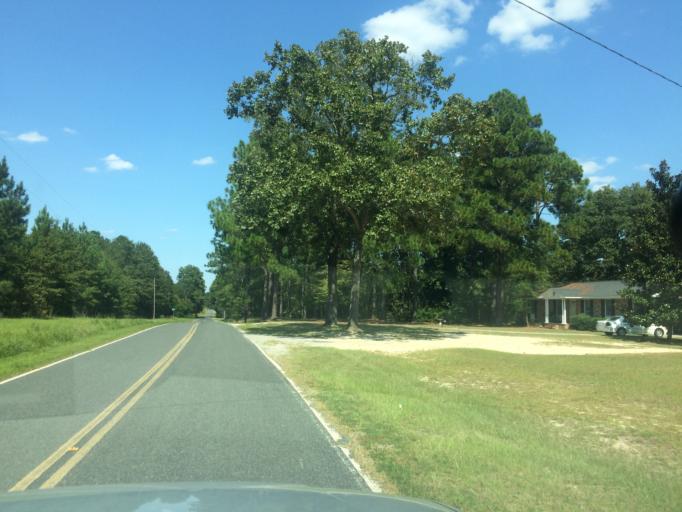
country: US
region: South Carolina
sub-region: Barnwell County
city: Williston
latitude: 33.6270
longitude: -81.4476
